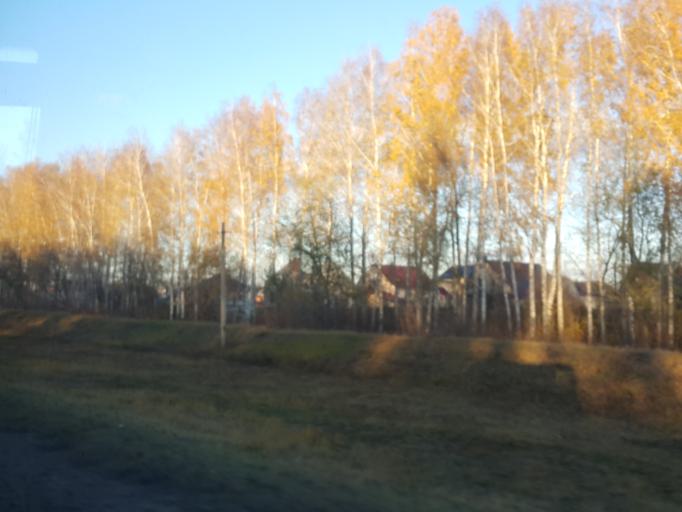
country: RU
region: Tambov
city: Bokino
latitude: 52.6196
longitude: 41.4439
